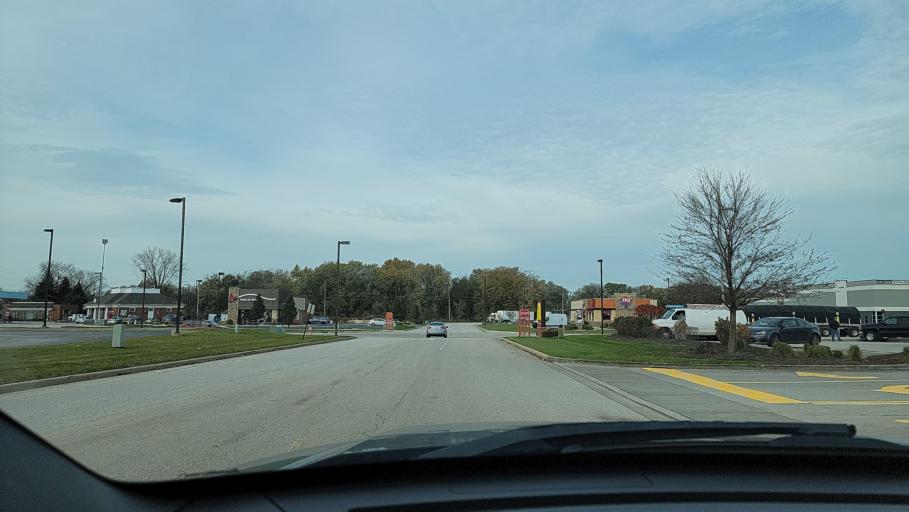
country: US
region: Indiana
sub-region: Porter County
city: Ogden Dunes
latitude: 41.6066
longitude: -87.1716
